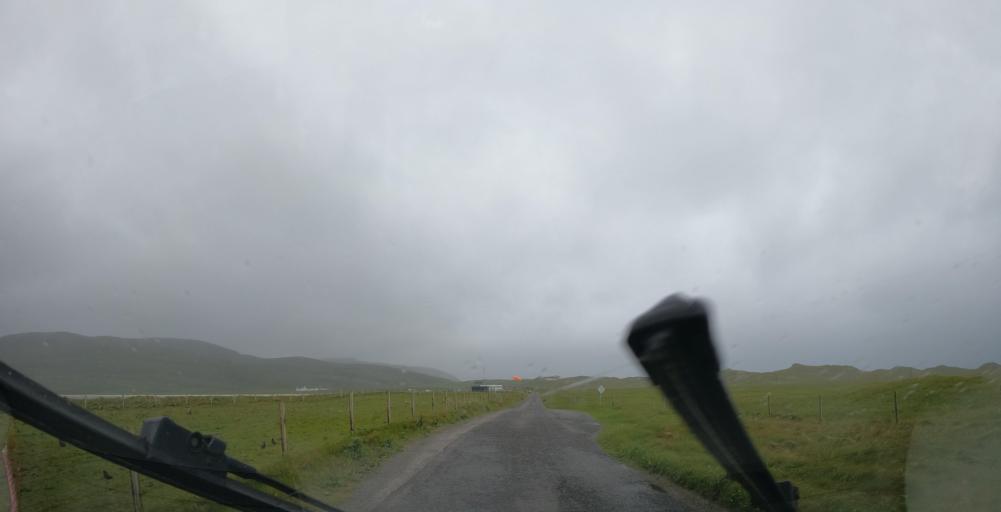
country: GB
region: Scotland
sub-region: Eilean Siar
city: Barra
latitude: 57.0269
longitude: -7.4444
